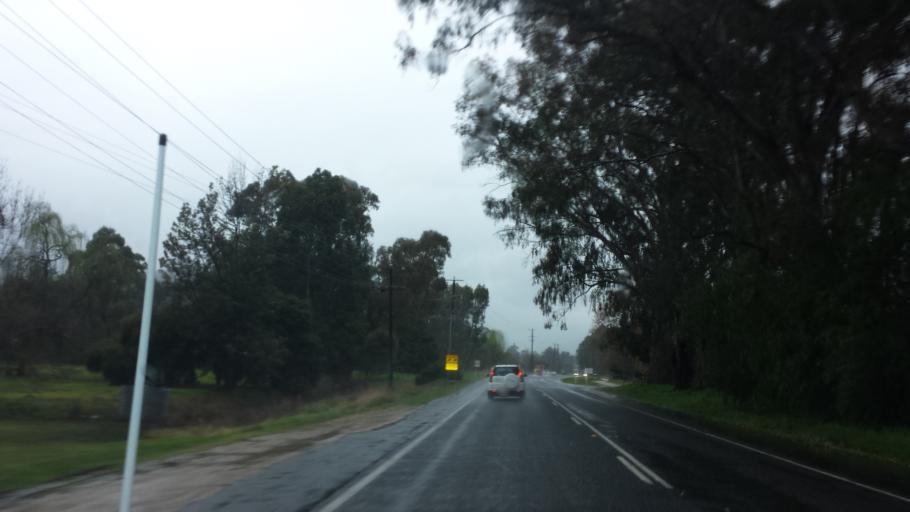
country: AU
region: Victoria
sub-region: Alpine
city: Mount Beauty
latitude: -36.5886
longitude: 146.7615
